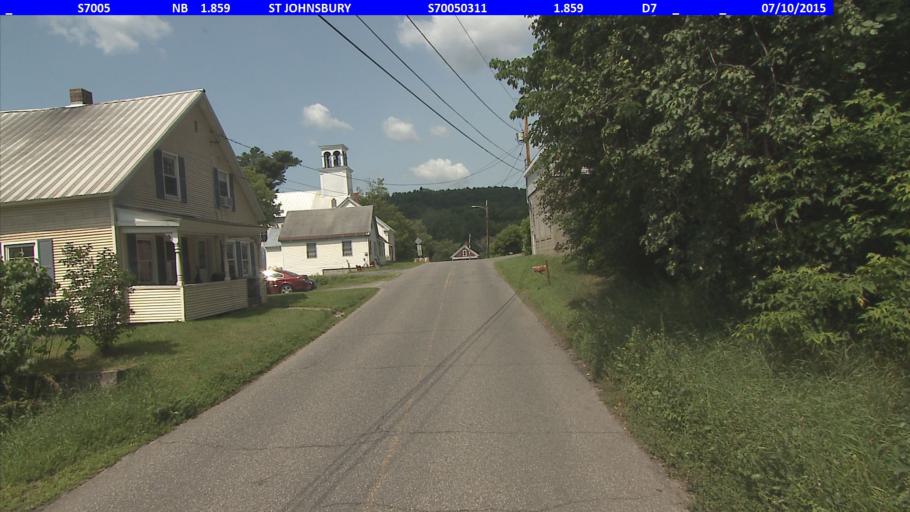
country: US
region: Vermont
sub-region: Caledonia County
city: St Johnsbury
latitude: 44.4558
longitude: -72.0140
